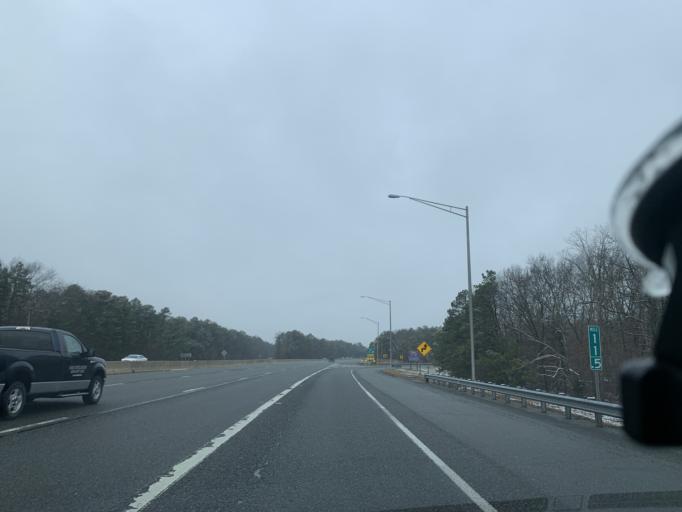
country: US
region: New Jersey
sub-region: Atlantic County
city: Pomona
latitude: 39.4464
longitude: -74.6195
